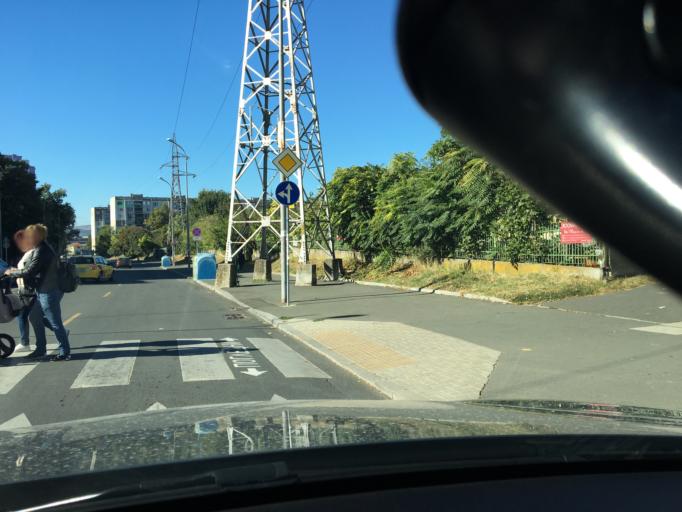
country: BG
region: Burgas
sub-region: Obshtina Burgas
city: Burgas
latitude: 42.5196
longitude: 27.4509
